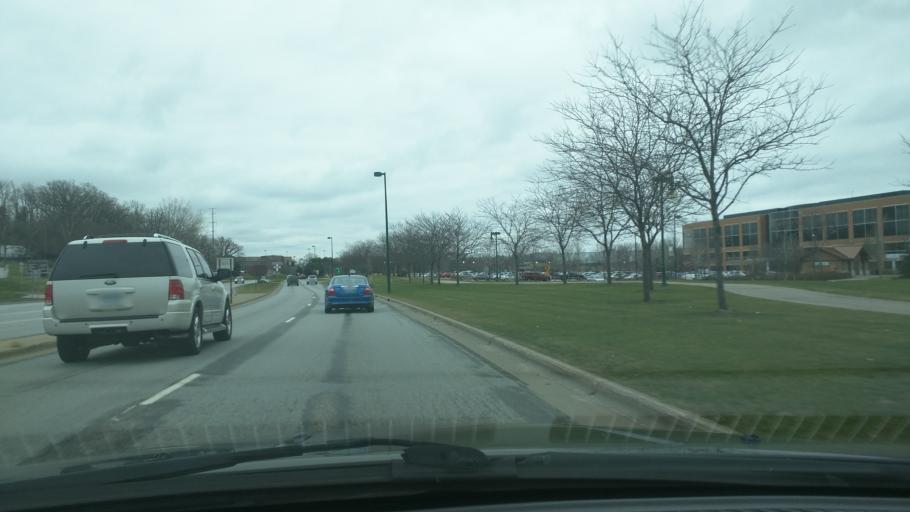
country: US
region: Minnesota
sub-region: Hennepin County
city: Eden Prairie
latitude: 44.8596
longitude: -93.4399
